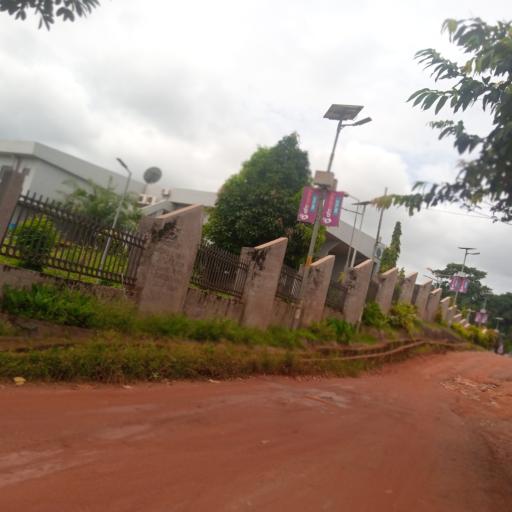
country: SL
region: Eastern Province
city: Kenema
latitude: 7.8780
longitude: -11.1950
